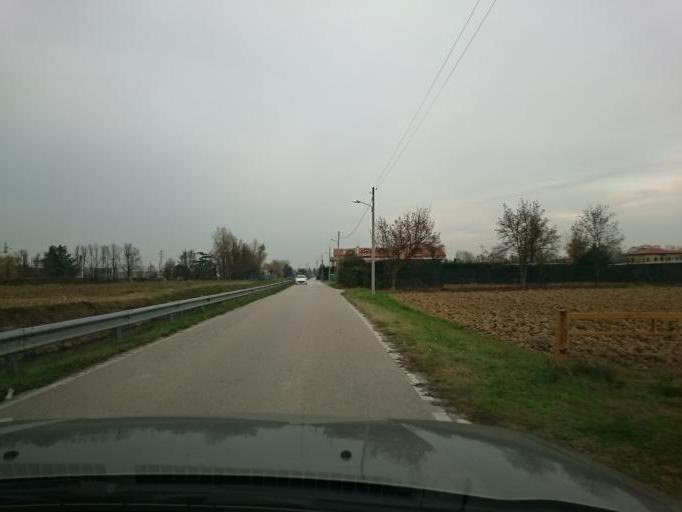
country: IT
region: Veneto
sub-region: Provincia di Padova
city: Caselle
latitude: 45.4008
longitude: 11.8235
